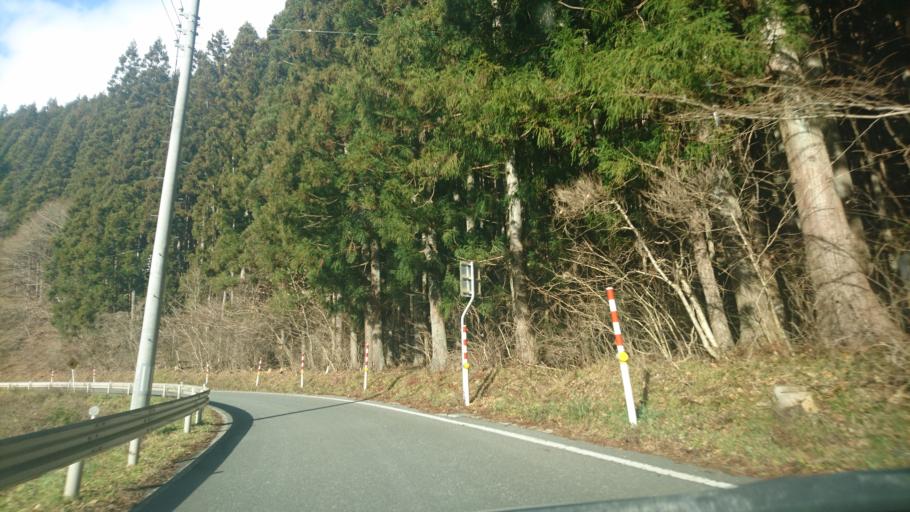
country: JP
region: Iwate
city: Mizusawa
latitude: 39.0986
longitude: 141.3840
